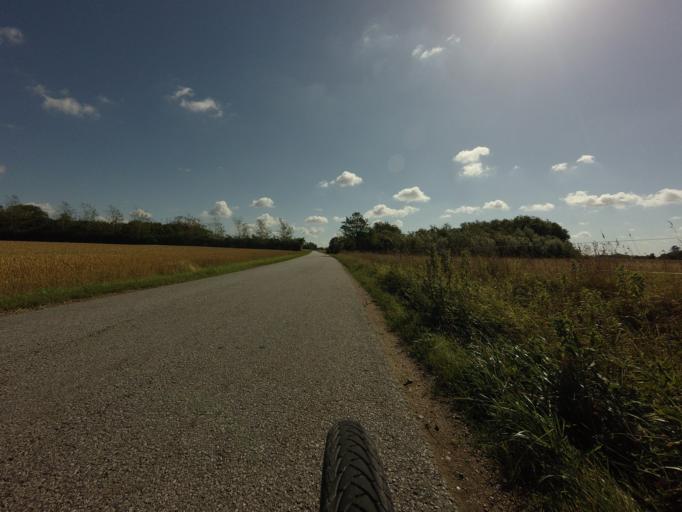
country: DK
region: North Denmark
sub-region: Hjorring Kommune
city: Hjorring
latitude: 57.4335
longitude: 9.8944
